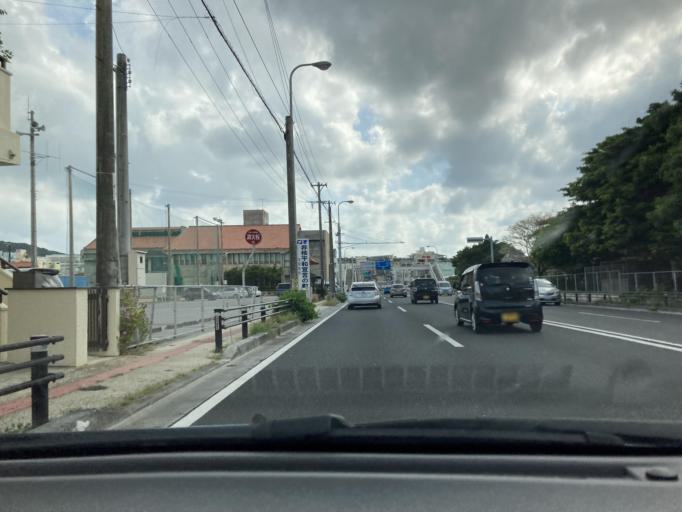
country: JP
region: Okinawa
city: Ginowan
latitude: 26.2047
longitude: 127.7556
